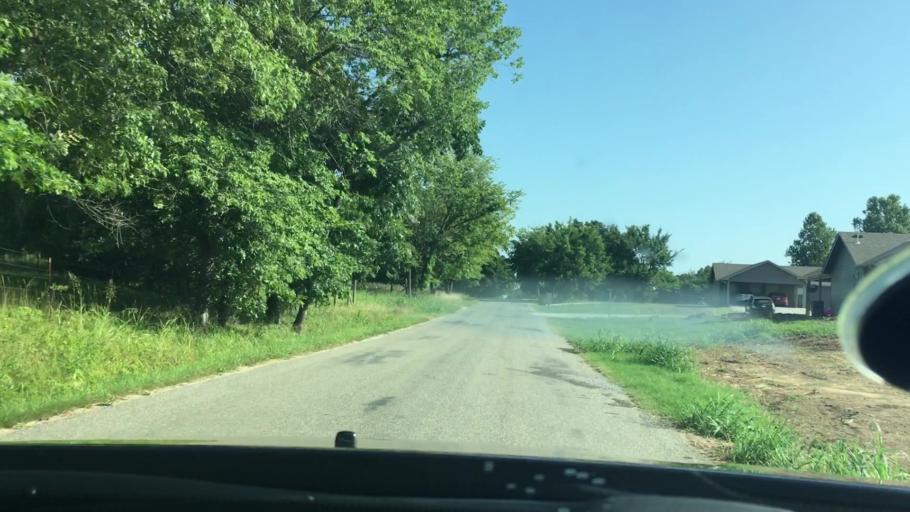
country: US
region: Oklahoma
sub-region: Pontotoc County
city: Byng
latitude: 34.8157
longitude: -96.6259
